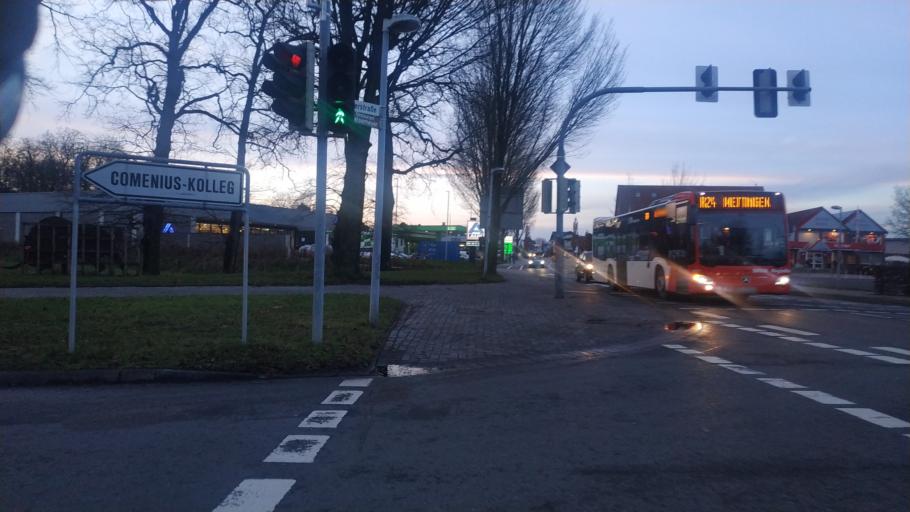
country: DE
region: North Rhine-Westphalia
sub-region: Regierungsbezirk Munster
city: Mettingen
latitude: 52.3184
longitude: 7.7787
